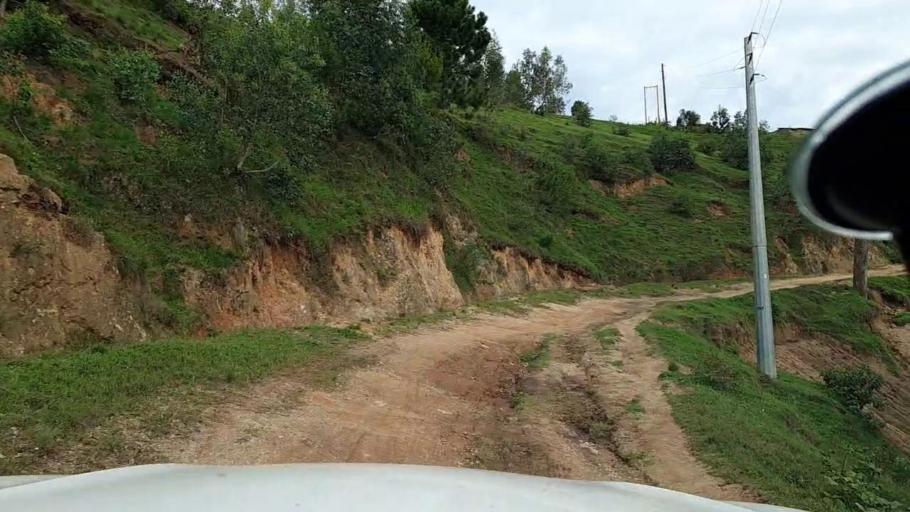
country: RW
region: Southern Province
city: Gitarama
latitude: -2.1250
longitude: 29.6541
